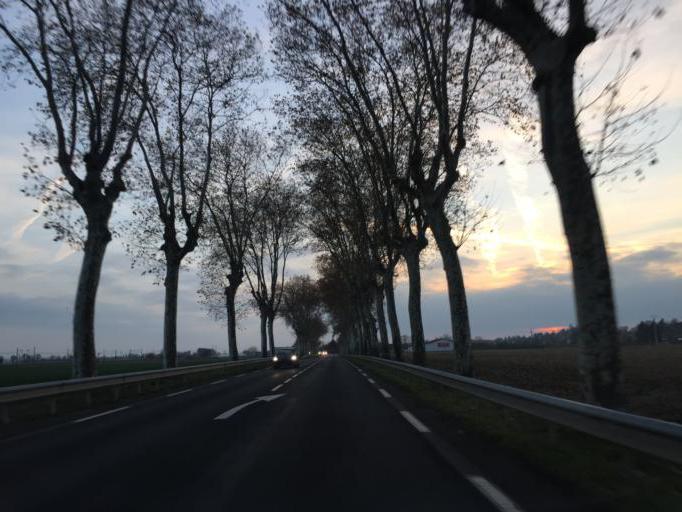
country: FR
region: Rhone-Alpes
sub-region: Departement de l'Ain
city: Perouges
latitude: 45.8925
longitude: 5.1782
